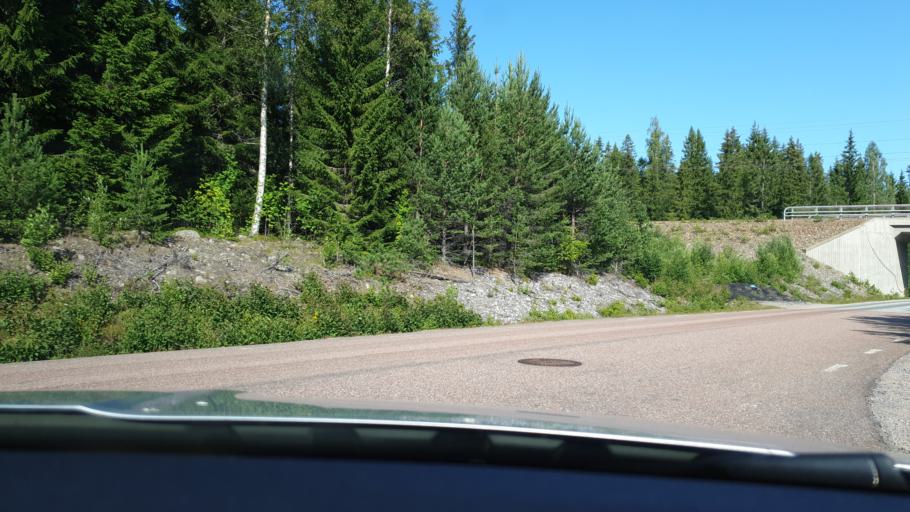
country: SE
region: Gaevleborg
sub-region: Soderhamns Kommun
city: Soderhamn
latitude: 61.4279
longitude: 16.9859
